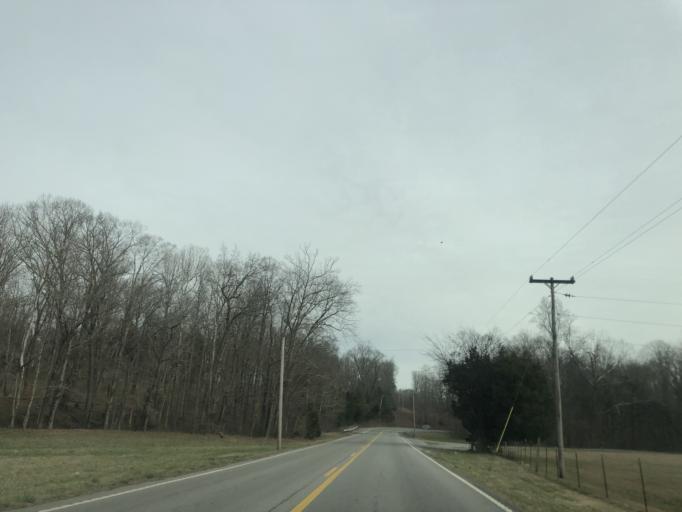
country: US
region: Tennessee
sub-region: Sumner County
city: White House
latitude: 36.5217
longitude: -86.6247
